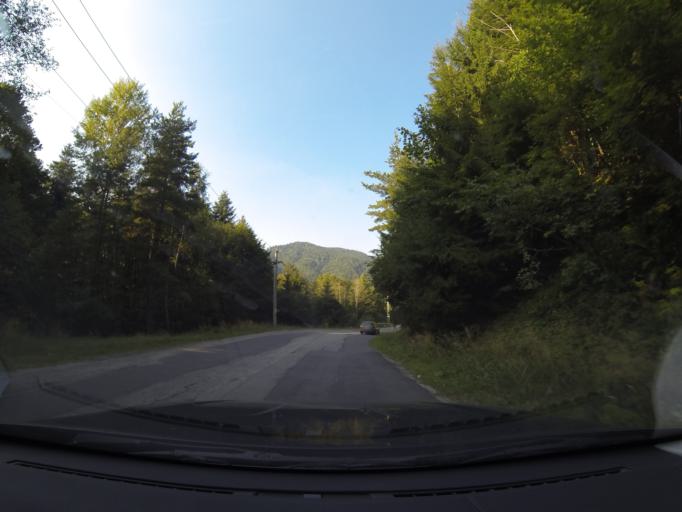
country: RO
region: Arges
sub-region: Comuna Arefu
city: Arefu
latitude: 45.3986
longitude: 24.6385
